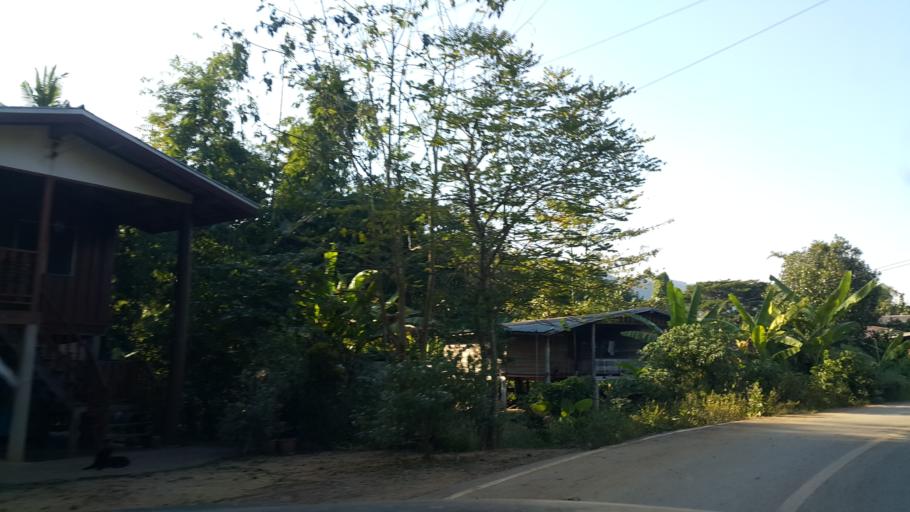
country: TH
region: Sukhothai
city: Thung Saliam
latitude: 17.4106
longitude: 99.5136
